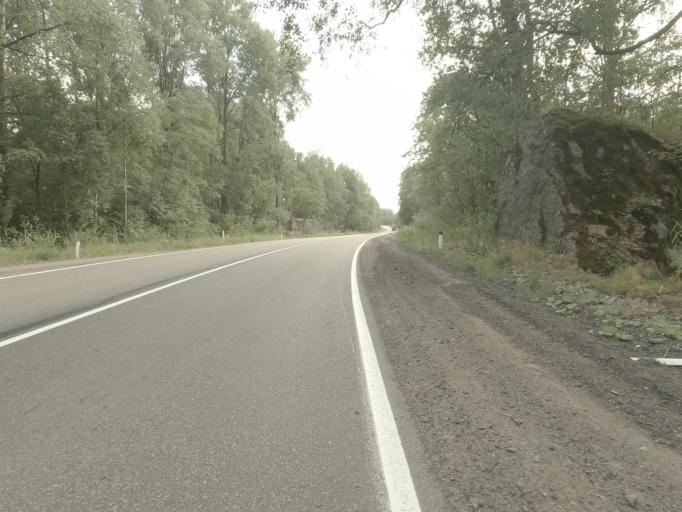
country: RU
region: Leningrad
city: Kamennogorsk
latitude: 60.8666
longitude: 28.9778
